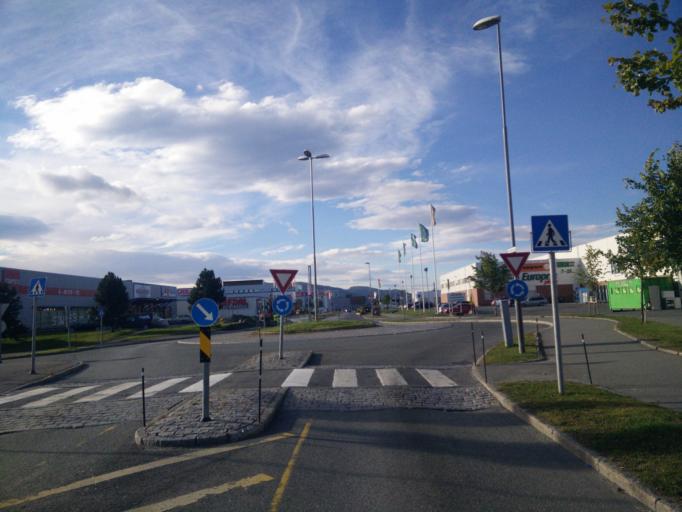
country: NO
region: Sor-Trondelag
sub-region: Trondheim
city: Trondheim
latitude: 63.3577
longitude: 10.3757
